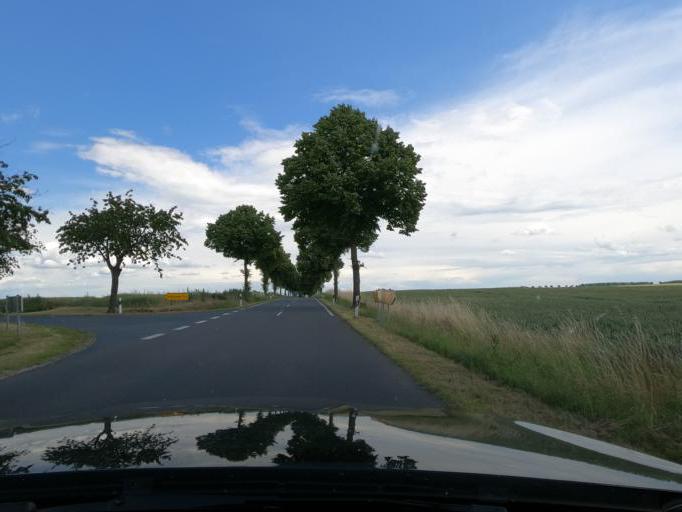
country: DE
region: Lower Saxony
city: Schellerten
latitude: 52.1762
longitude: 10.1402
